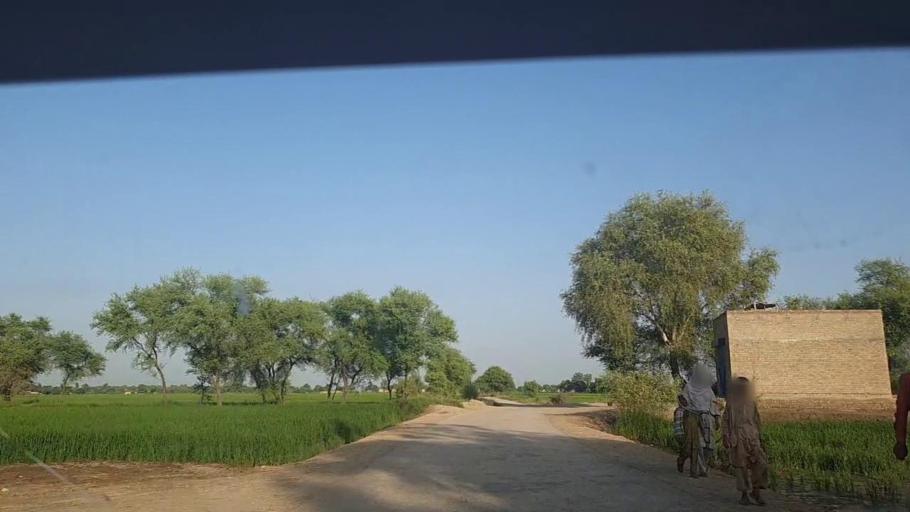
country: PK
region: Sindh
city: Thul
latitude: 28.2159
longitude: 68.8688
